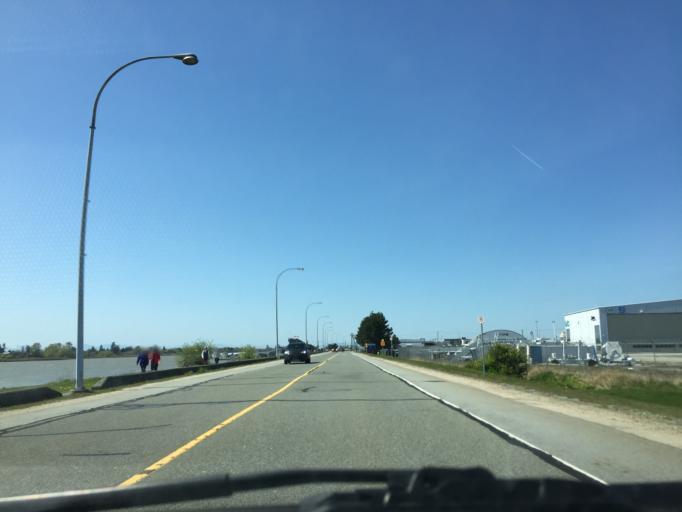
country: CA
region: British Columbia
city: Richmond
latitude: 49.1778
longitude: -123.1625
